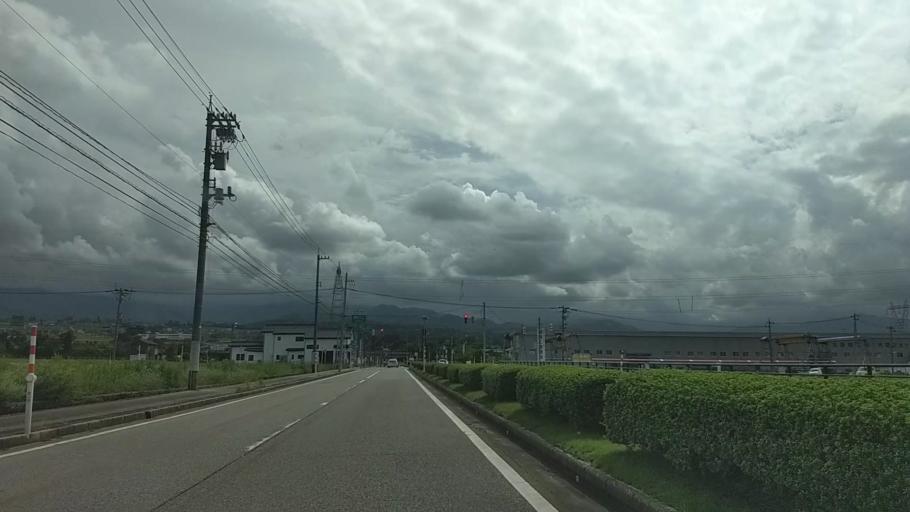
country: JP
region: Toyama
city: Namerikawa
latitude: 36.7465
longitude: 137.3761
